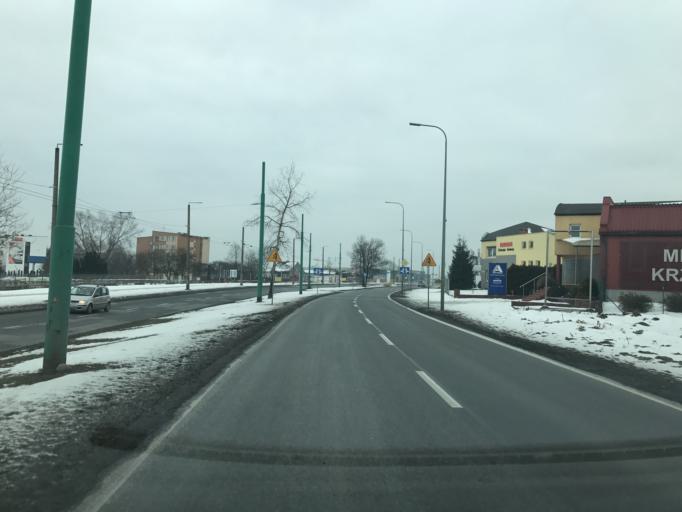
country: PL
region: Silesian Voivodeship
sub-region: Tychy
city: Cielmice
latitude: 50.1020
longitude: 19.0303
